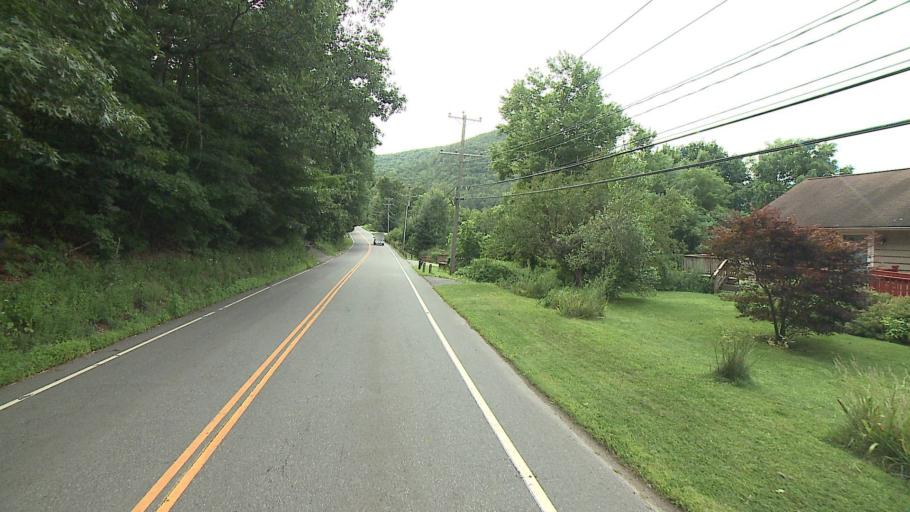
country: US
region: Connecticut
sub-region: Litchfield County
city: Kent
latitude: 41.7159
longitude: -73.4702
